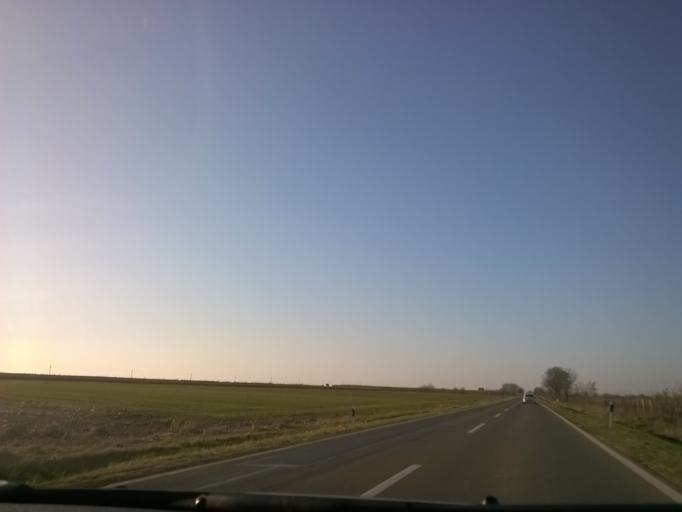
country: RS
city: Banatski Karlovac
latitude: 45.0594
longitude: 20.9898
